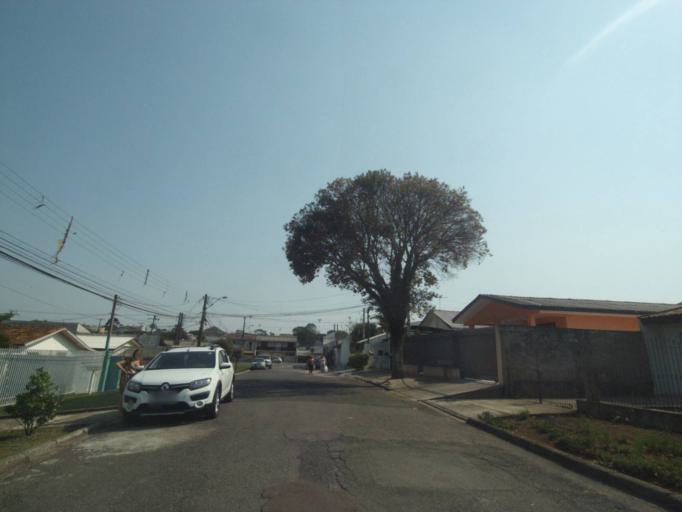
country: BR
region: Parana
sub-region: Sao Jose Dos Pinhais
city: Sao Jose dos Pinhais
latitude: -25.5147
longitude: -49.2725
